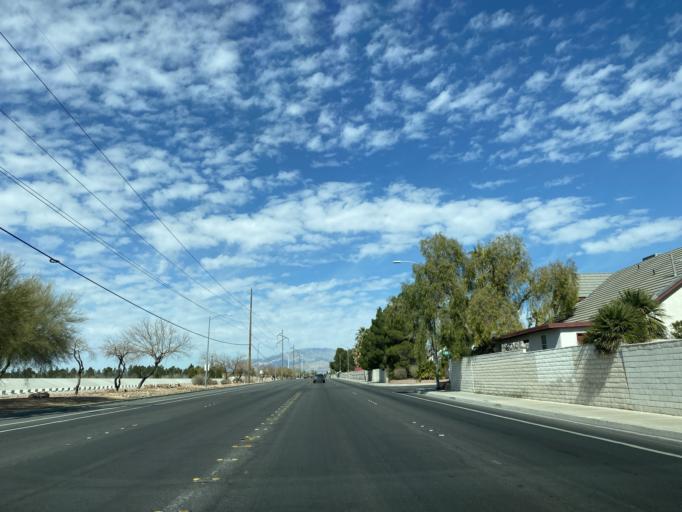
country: US
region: Nevada
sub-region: Clark County
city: Spring Valley
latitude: 36.2275
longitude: -115.2514
